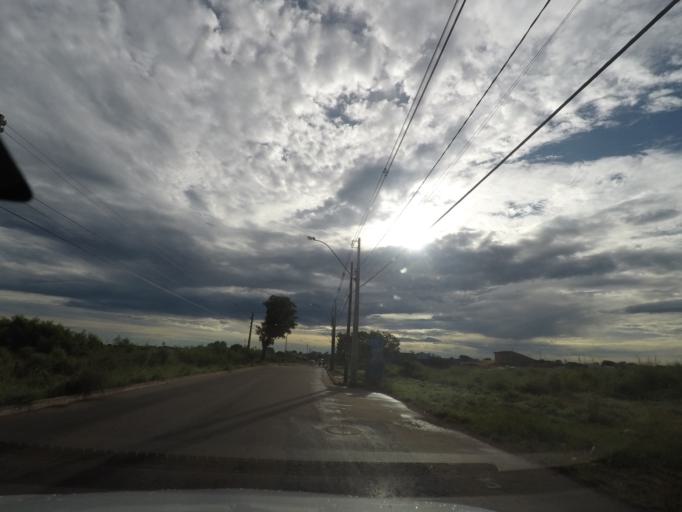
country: BR
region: Goias
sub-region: Aparecida De Goiania
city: Aparecida de Goiania
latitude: -16.7611
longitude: -49.3574
